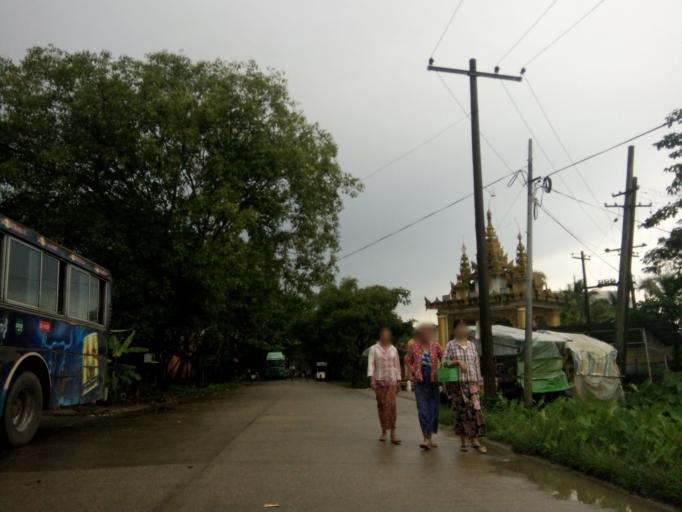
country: MM
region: Yangon
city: Yangon
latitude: 16.9181
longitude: 96.1590
